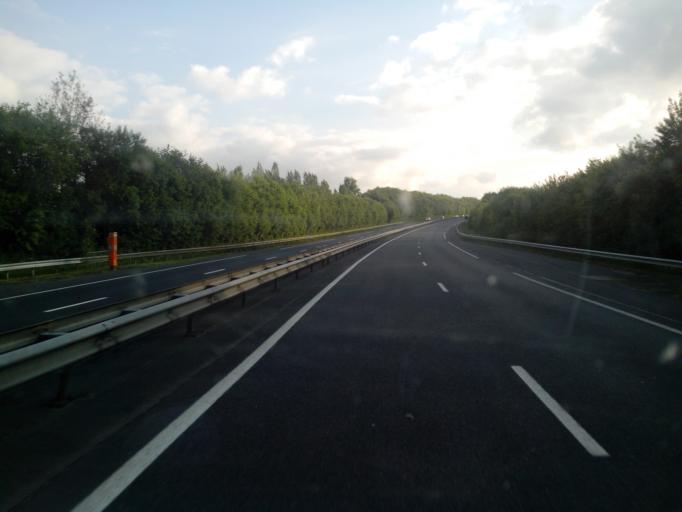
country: FR
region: Lower Normandy
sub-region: Departement du Calvados
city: Saint-Martin-des-Besaces
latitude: 49.0167
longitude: -0.8479
